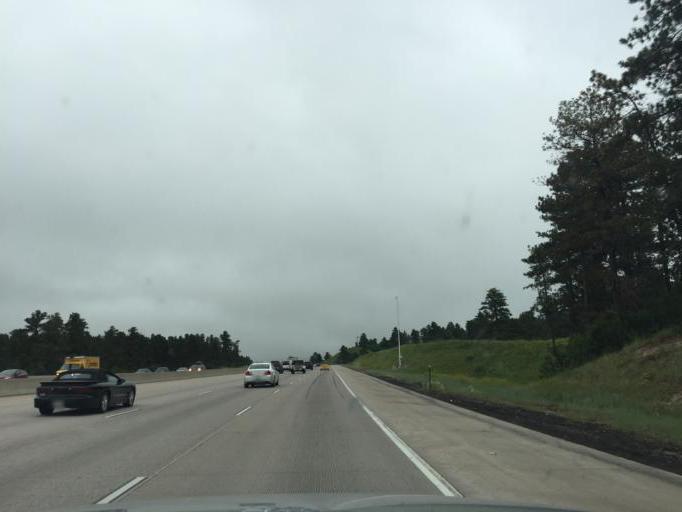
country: US
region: Colorado
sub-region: Douglas County
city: Castle Pines
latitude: 39.4373
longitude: -104.8778
